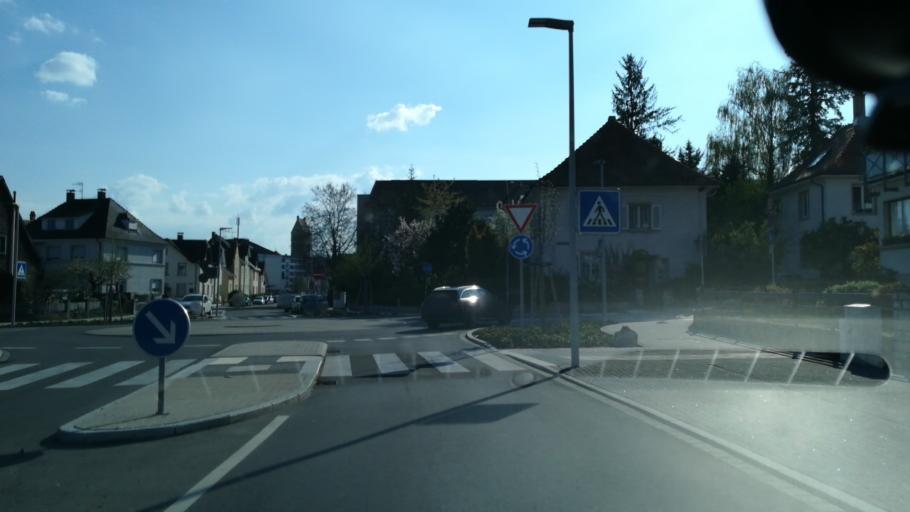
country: DE
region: Baden-Wuerttemberg
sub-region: Freiburg Region
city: Singen
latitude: 47.7658
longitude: 8.8469
